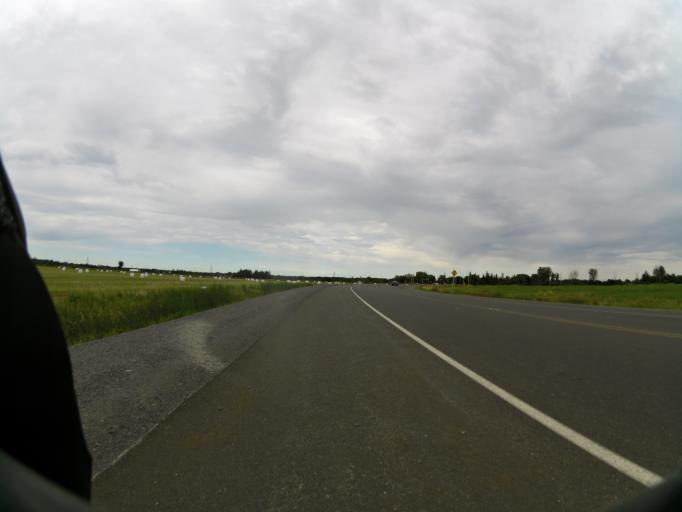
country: CA
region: Ontario
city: Ottawa
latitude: 45.3062
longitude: -75.7132
